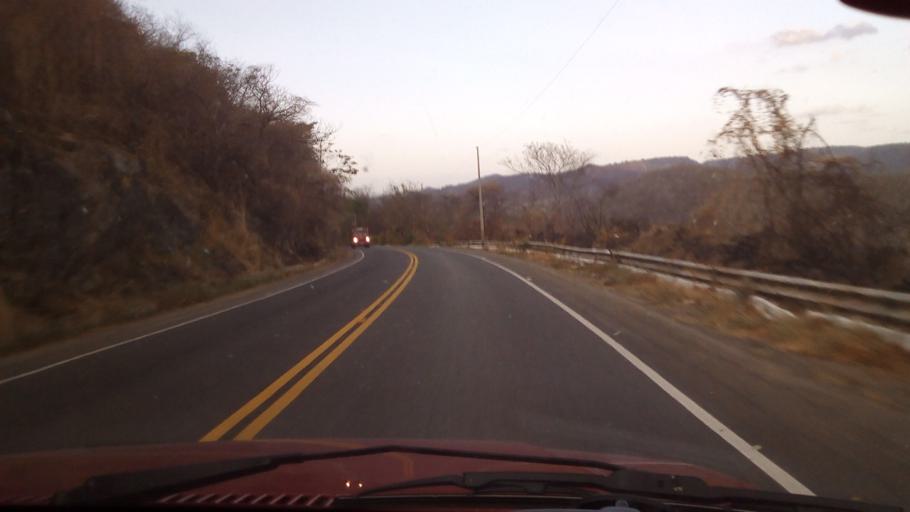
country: BR
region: Paraiba
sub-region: Bananeiras
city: Solanea
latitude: -6.7355
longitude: -35.5570
